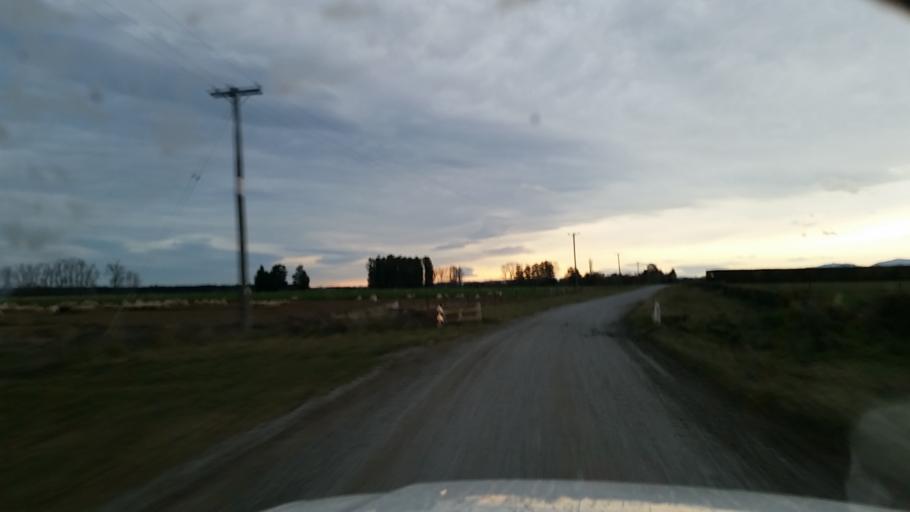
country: NZ
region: Canterbury
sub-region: Ashburton District
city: Ashburton
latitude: -43.8284
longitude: 171.6345
